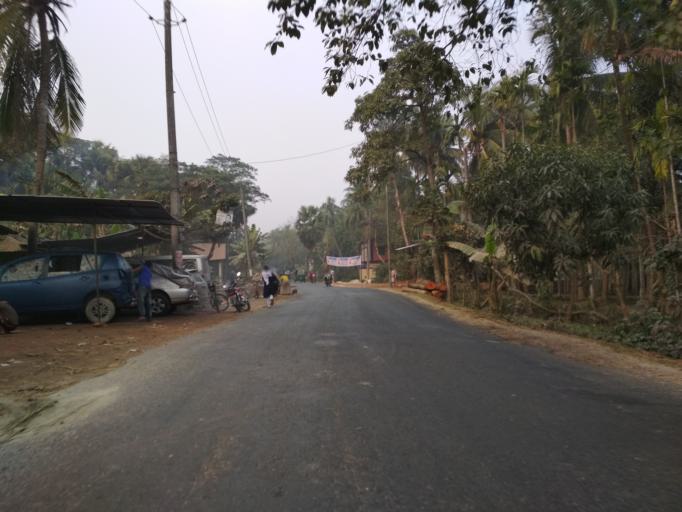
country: BD
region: Chittagong
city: Lakshmipur
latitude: 22.9261
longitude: 90.8339
